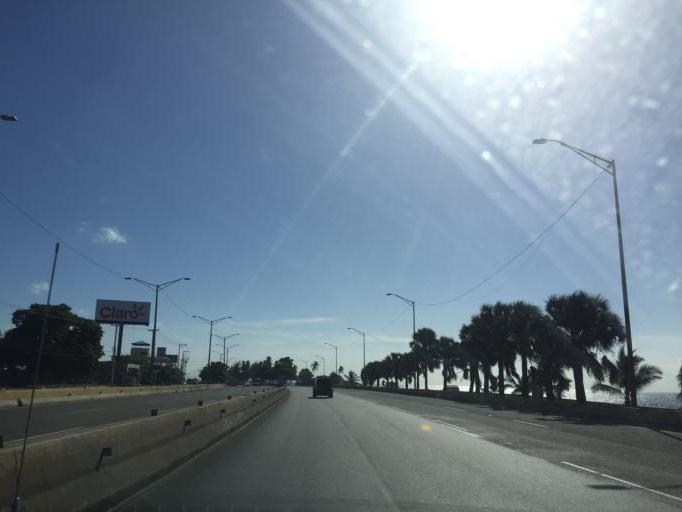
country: DO
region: Santo Domingo
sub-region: Santo Domingo
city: Santo Domingo Este
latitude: 18.4682
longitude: -69.8279
